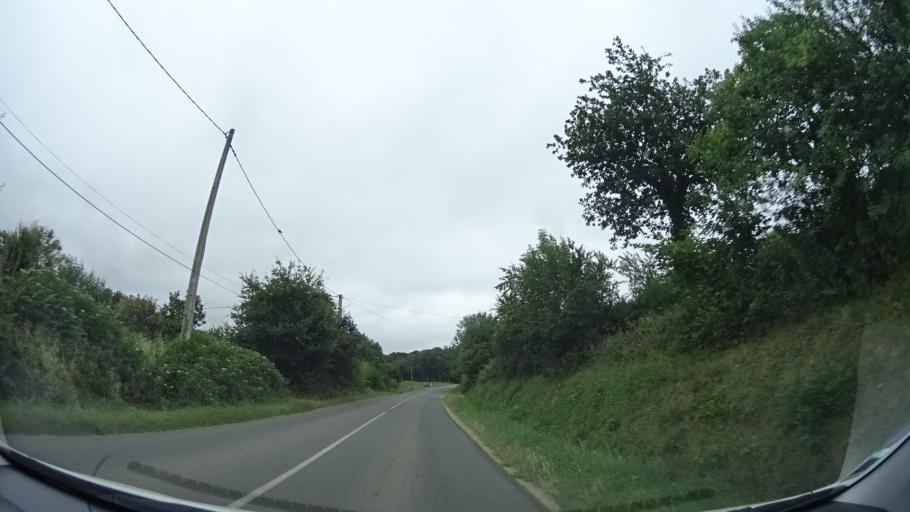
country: FR
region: Brittany
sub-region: Departement d'Ille-et-Vilaine
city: Pleugueneuc
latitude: 48.3496
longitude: -1.9268
